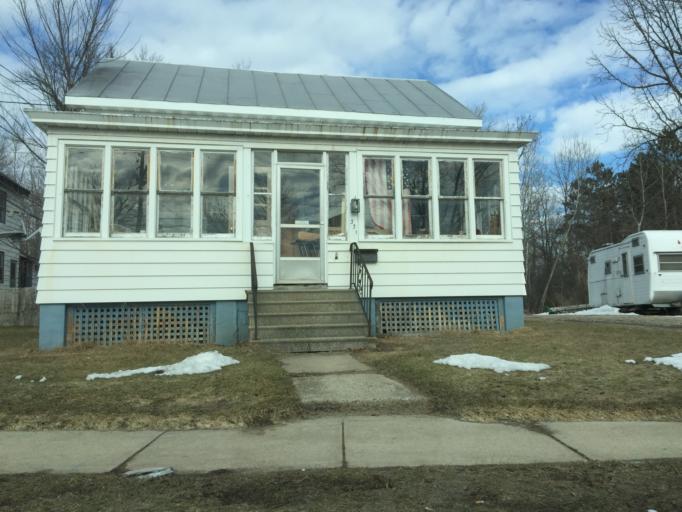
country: US
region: Wisconsin
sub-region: Oconto County
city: Oconto
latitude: 44.8922
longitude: -87.8807
